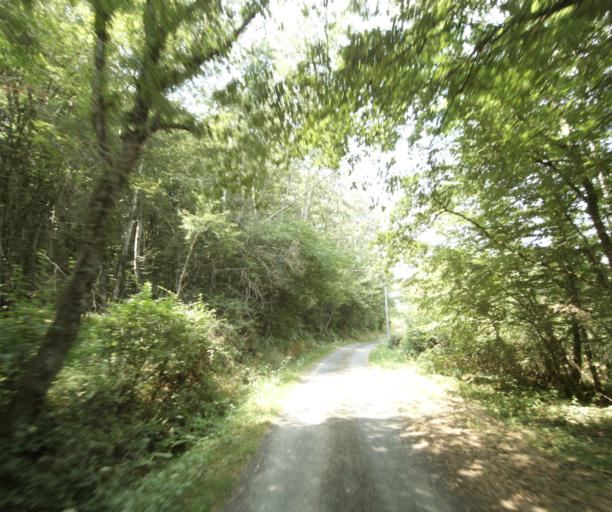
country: FR
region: Bourgogne
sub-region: Departement de Saone-et-Loire
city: Gueugnon
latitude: 46.6055
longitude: 4.0210
